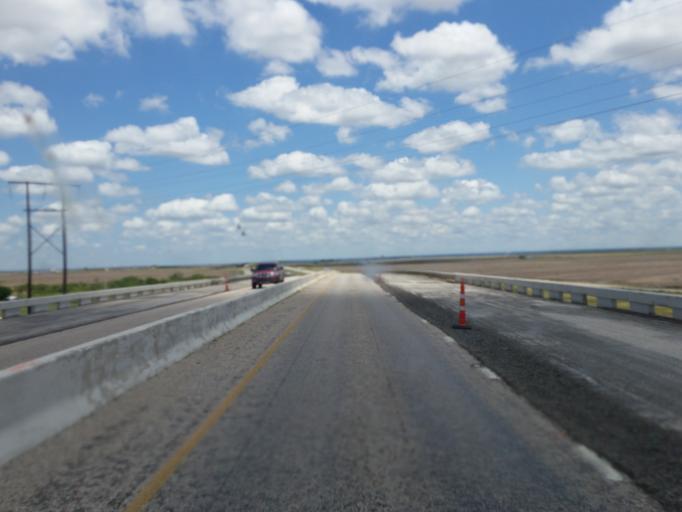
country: US
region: Texas
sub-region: Nolan County
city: Roscoe
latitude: 32.4499
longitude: -100.5202
